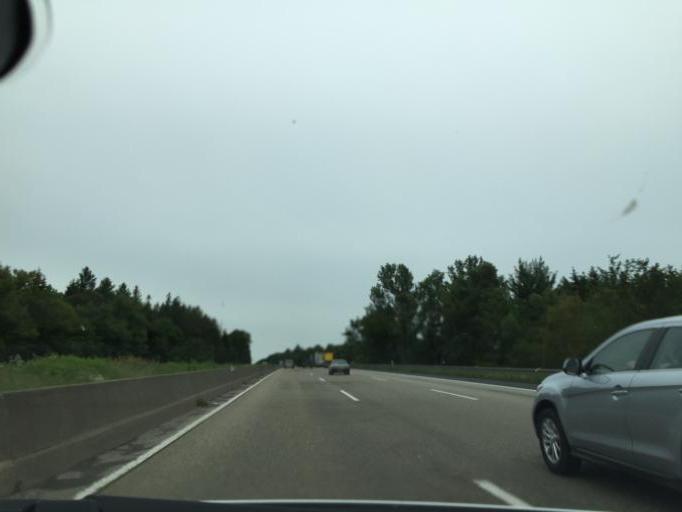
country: DE
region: Bavaria
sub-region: Regierungsbezirk Unterfranken
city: Motten
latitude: 50.3773
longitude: 9.7334
